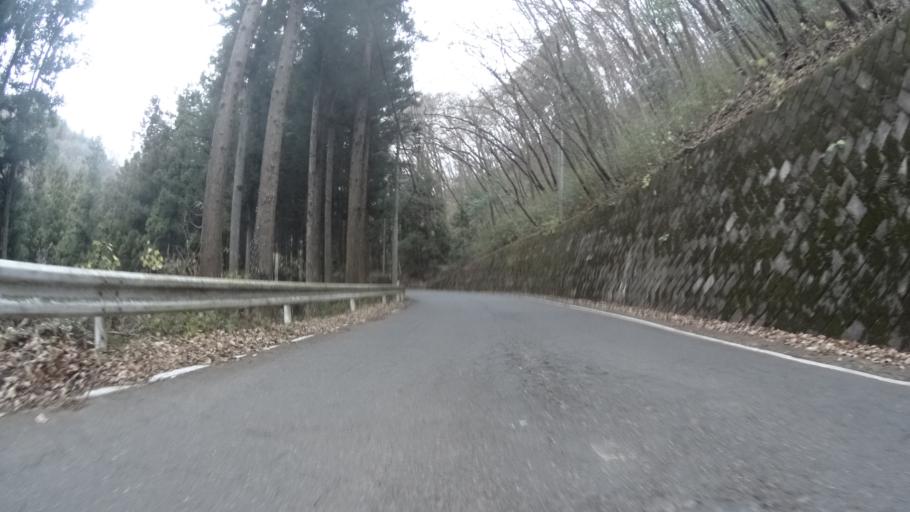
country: JP
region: Yamanashi
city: Uenohara
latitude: 35.6375
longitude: 139.1262
